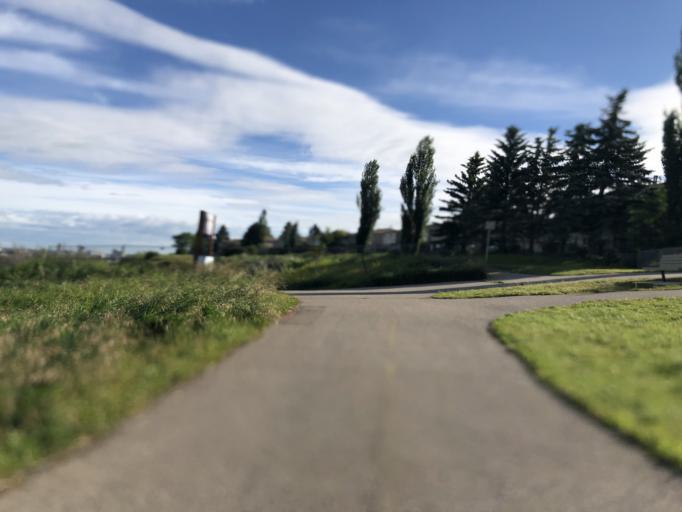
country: CA
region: Alberta
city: Calgary
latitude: 50.9973
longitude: -114.0228
